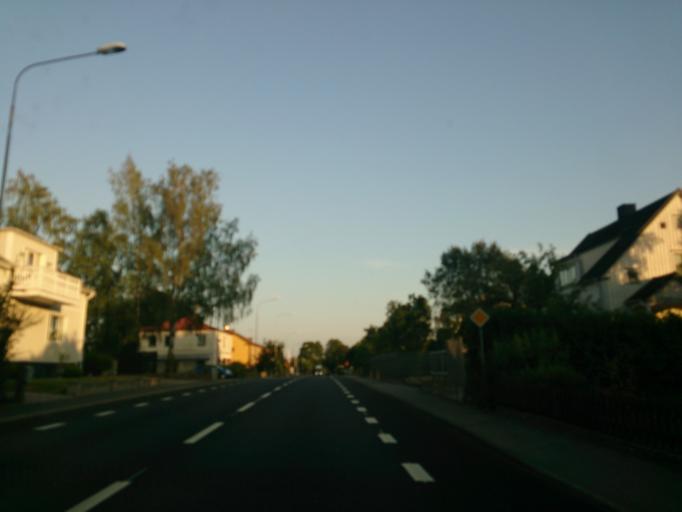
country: SE
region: Joenkoeping
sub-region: Varnamo Kommun
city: Bor
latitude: 57.1164
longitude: 14.1657
